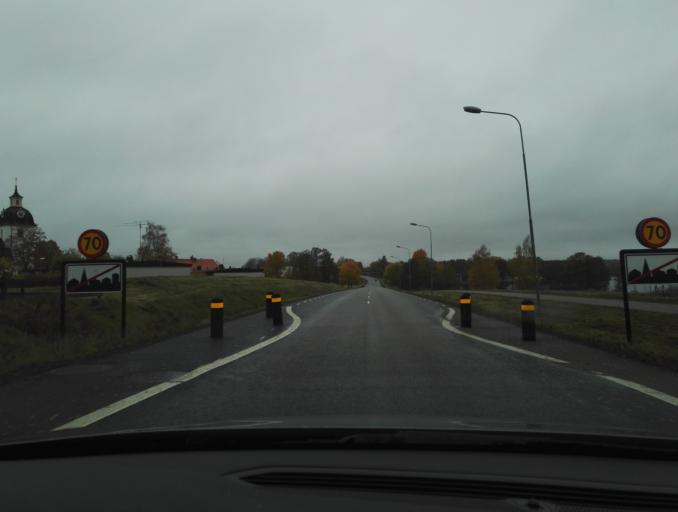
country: SE
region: Kronoberg
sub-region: Vaxjo Kommun
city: Rottne
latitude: 57.0275
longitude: 14.8907
